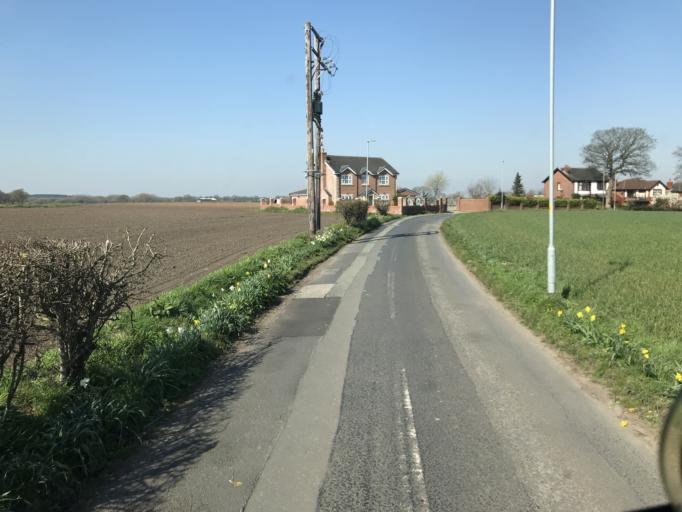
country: GB
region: England
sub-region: Trafford
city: Partington
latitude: 53.4174
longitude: -2.4592
